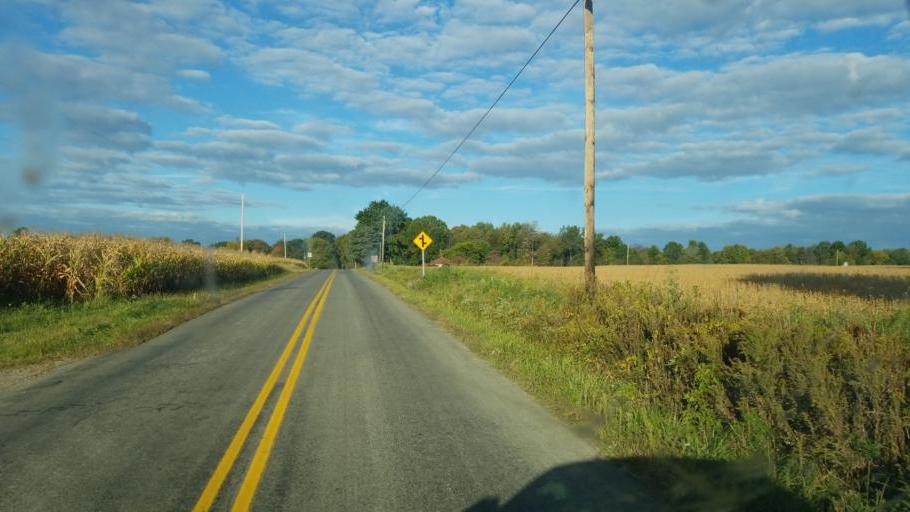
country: US
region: Pennsylvania
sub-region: Mercer County
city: Mercer
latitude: 41.3493
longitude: -80.2432
